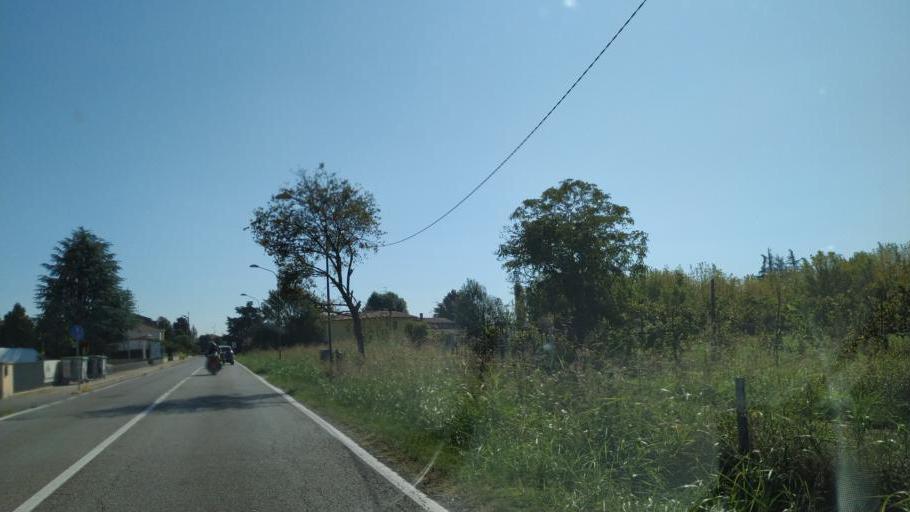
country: IT
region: Emilia-Romagna
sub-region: Provincia di Ferrara
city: San Carlo
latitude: 44.8000
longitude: 11.4064
